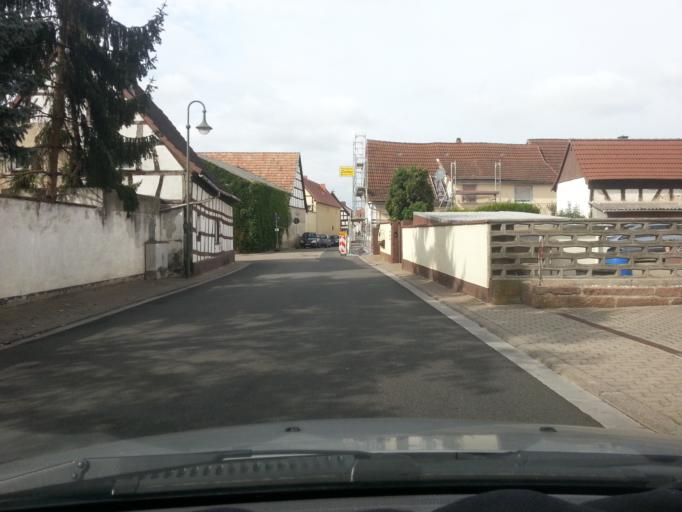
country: DE
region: Rheinland-Pfalz
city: Lachen-Speyerdorf
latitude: 49.3210
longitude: 8.2002
